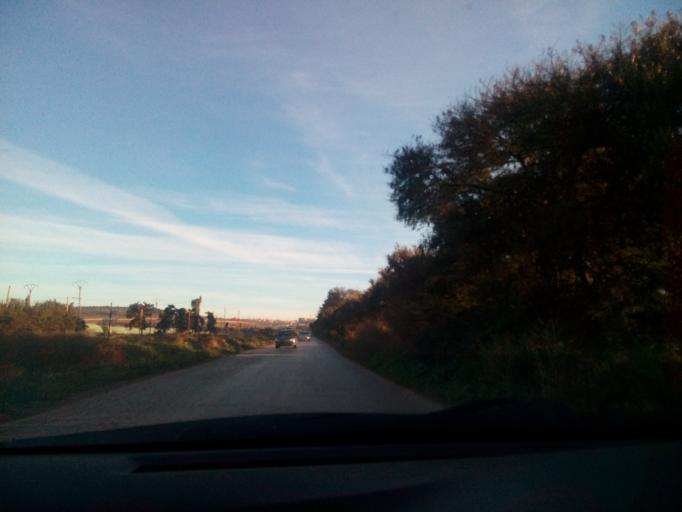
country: DZ
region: Oran
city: Es Senia
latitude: 35.6151
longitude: -0.6856
